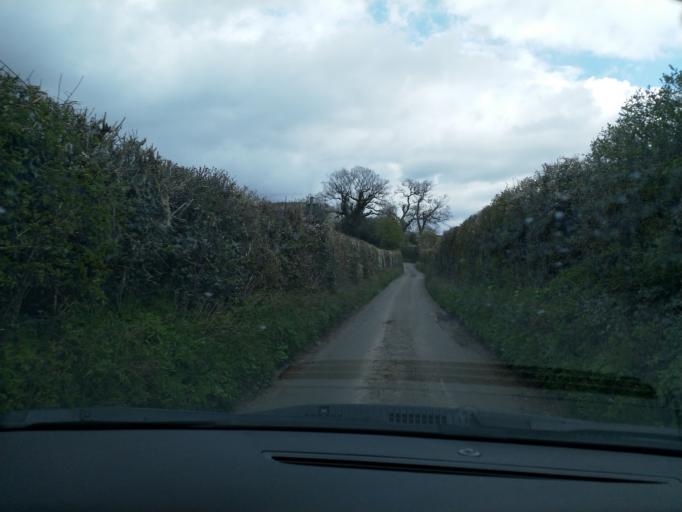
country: GB
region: England
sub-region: Warwickshire
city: Henley in Arden
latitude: 52.2901
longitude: -1.7461
